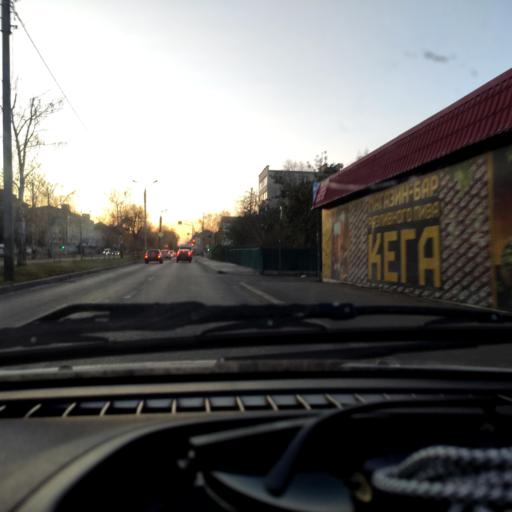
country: RU
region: Samara
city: Tol'yatti
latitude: 53.5195
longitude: 49.4027
